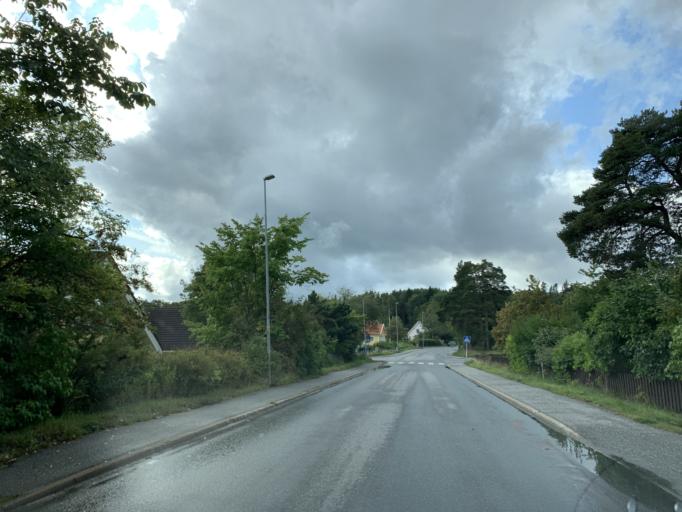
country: SE
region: Stockholm
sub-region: Taby Kommun
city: Taby
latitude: 59.4385
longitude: 18.0284
